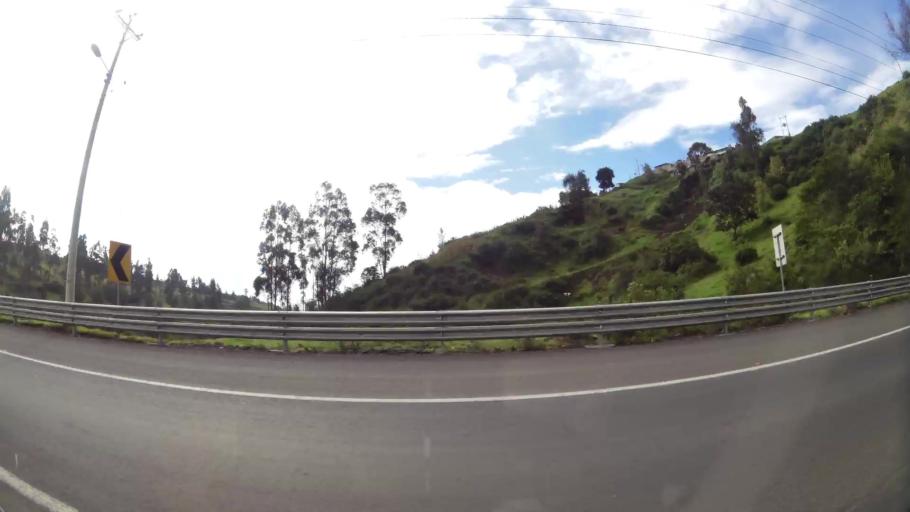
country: EC
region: Pichincha
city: Sangolqui
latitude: -0.3221
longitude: -78.4053
